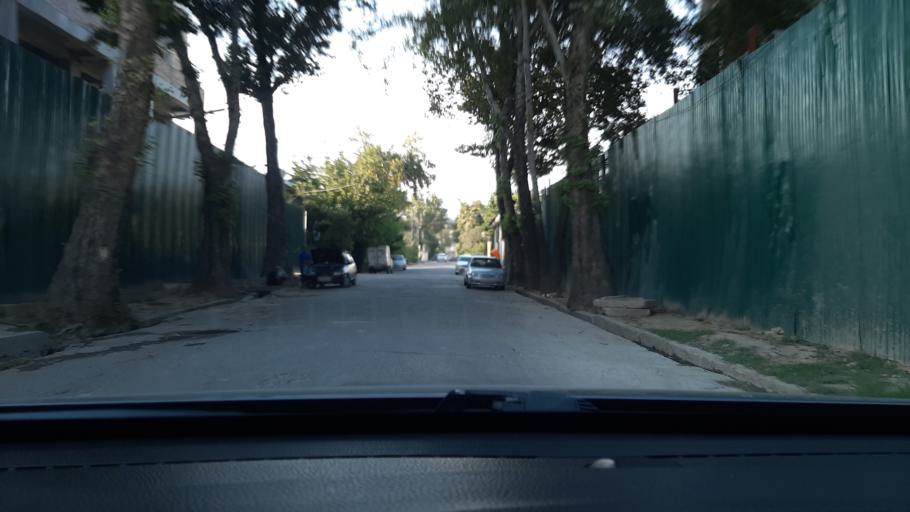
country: TJ
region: Dushanbe
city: Dushanbe
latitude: 38.5633
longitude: 68.8118
